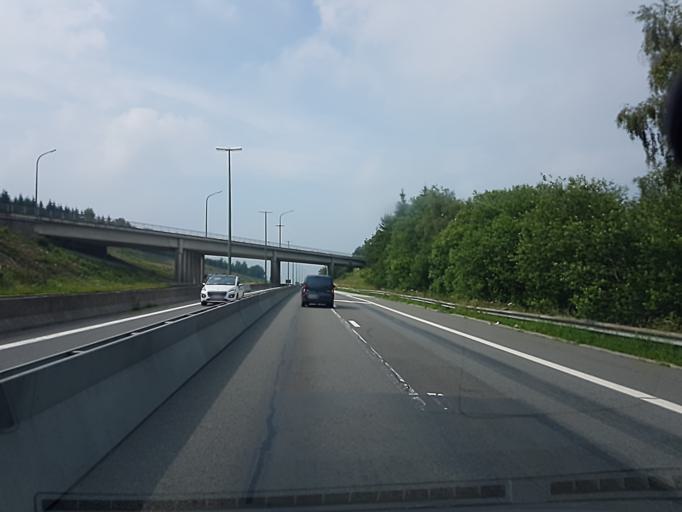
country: BE
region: Wallonia
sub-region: Province du Luxembourg
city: Manhay
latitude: 50.3632
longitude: 5.6733
